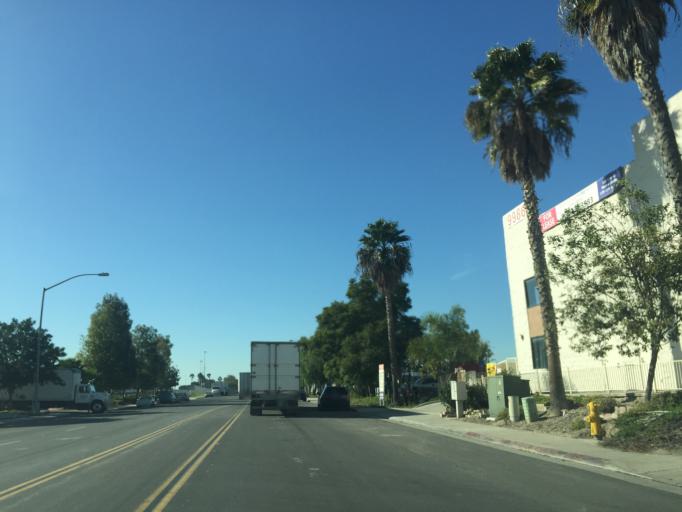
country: MX
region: Baja California
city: Tijuana
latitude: 32.5528
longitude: -116.9298
